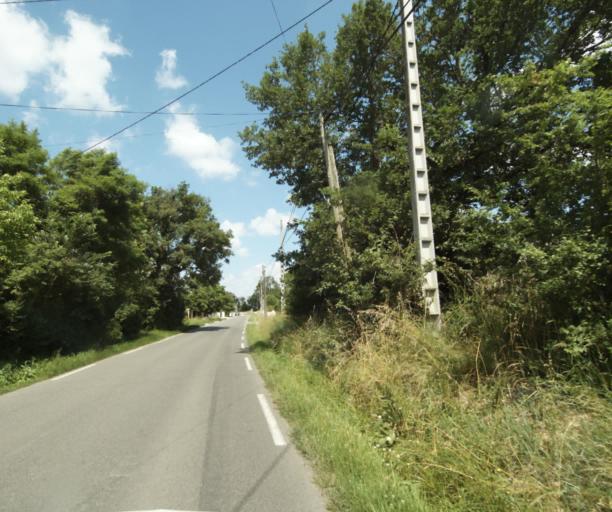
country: FR
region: Midi-Pyrenees
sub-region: Departement du Tarn-et-Garonne
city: Montauban
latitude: 44.0387
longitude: 1.3491
